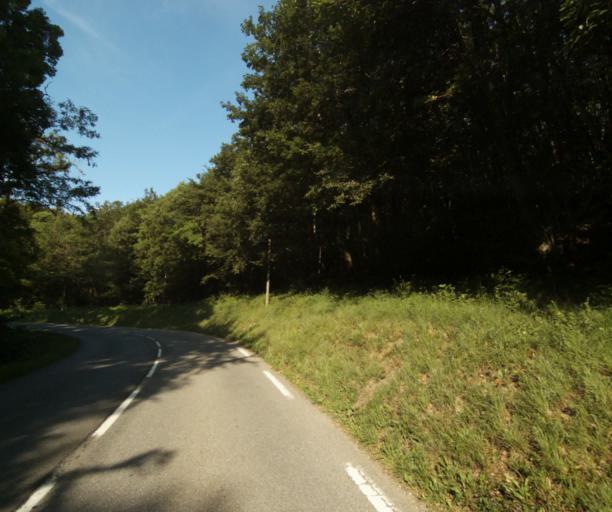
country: FR
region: Rhone-Alpes
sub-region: Departement de la Haute-Savoie
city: Armoy
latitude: 46.3587
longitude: 6.5148
